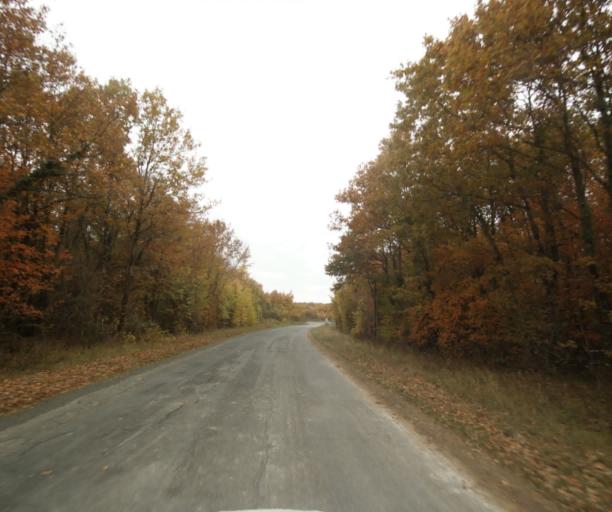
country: FR
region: Poitou-Charentes
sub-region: Departement de la Charente-Maritime
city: Chermignac
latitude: 45.7141
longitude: -0.6628
